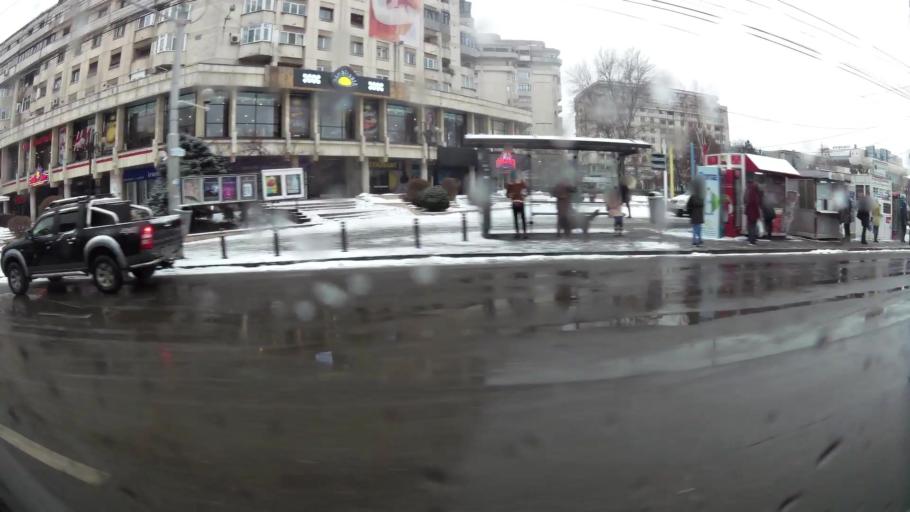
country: RO
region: Prahova
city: Ploiesti
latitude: 44.9418
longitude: 26.0209
